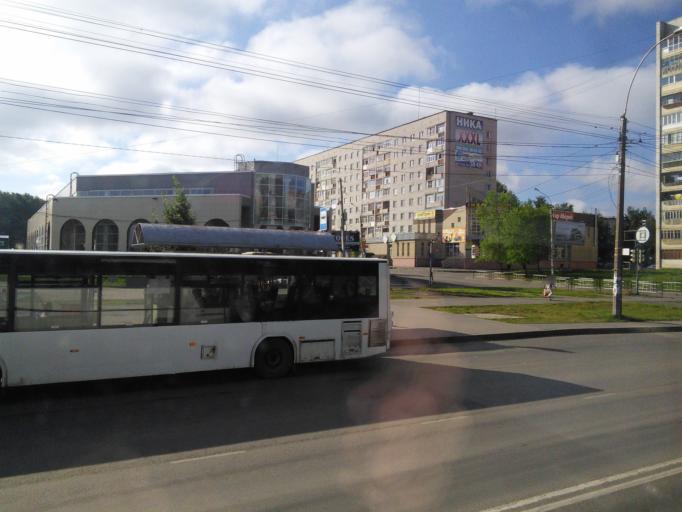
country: RU
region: Vologda
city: Vologda
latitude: 59.2047
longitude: 39.8359
